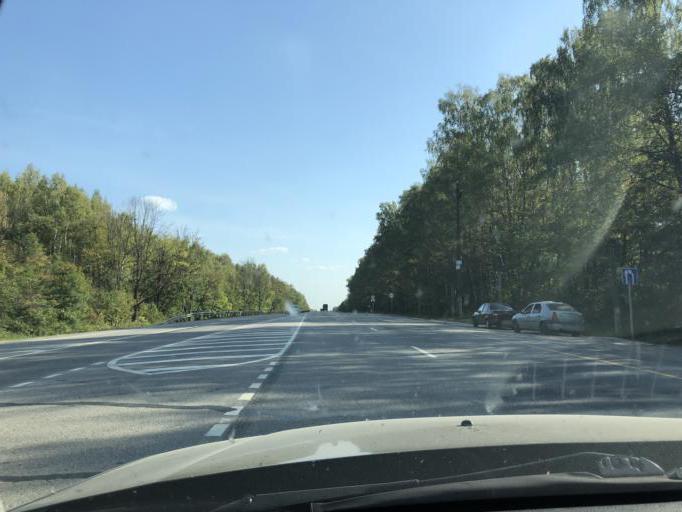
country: RU
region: Tula
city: Leninskiy
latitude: 54.3771
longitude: 37.5192
